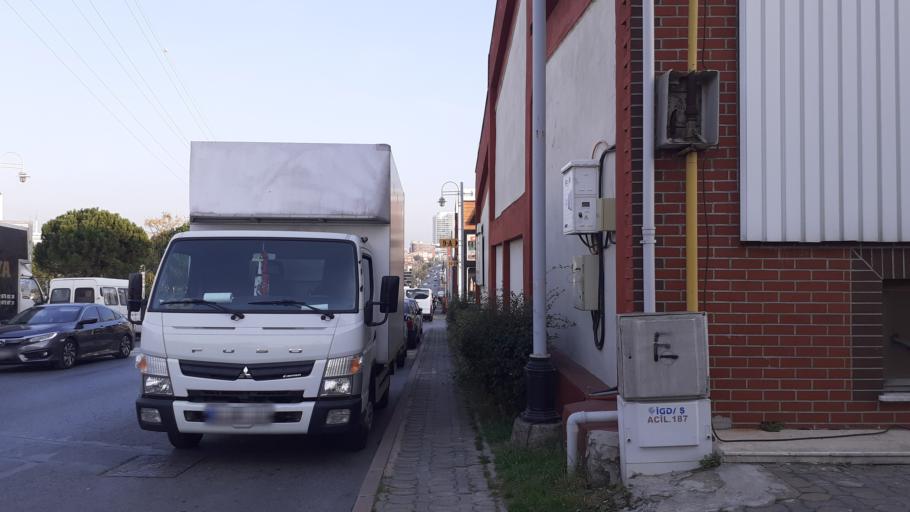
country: TR
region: Istanbul
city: Basaksehir
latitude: 41.0668
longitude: 28.7934
